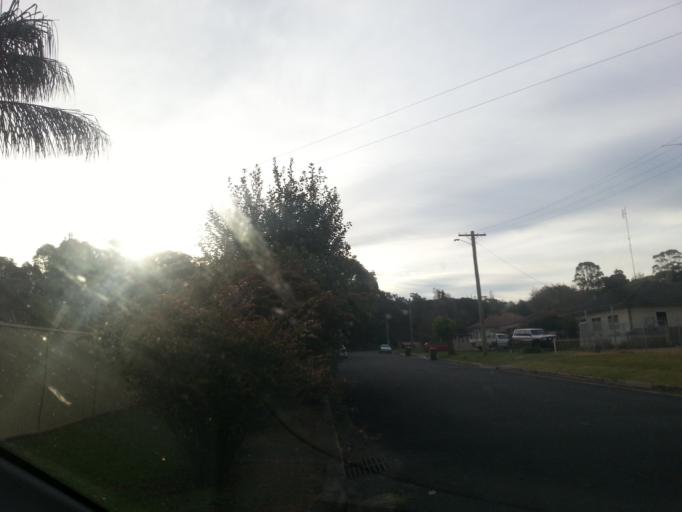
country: AU
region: New South Wales
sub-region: Wollongong
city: Lake Heights
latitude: -34.4753
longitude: 150.8709
